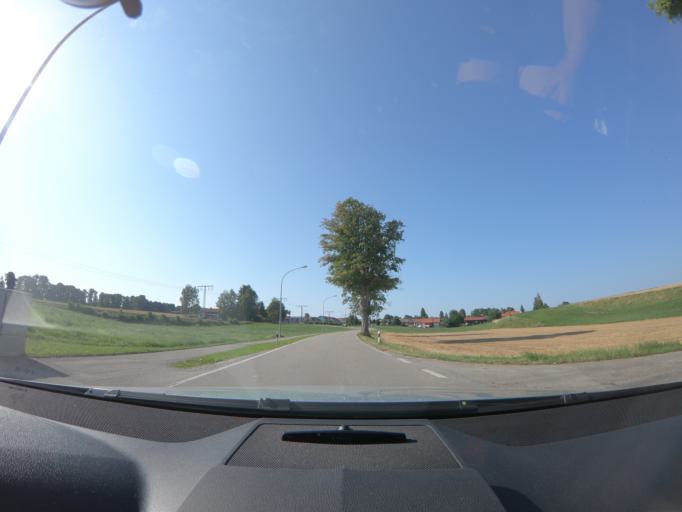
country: DE
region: Bavaria
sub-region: Upper Bavaria
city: Holzkirchen
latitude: 47.8710
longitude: 11.7087
